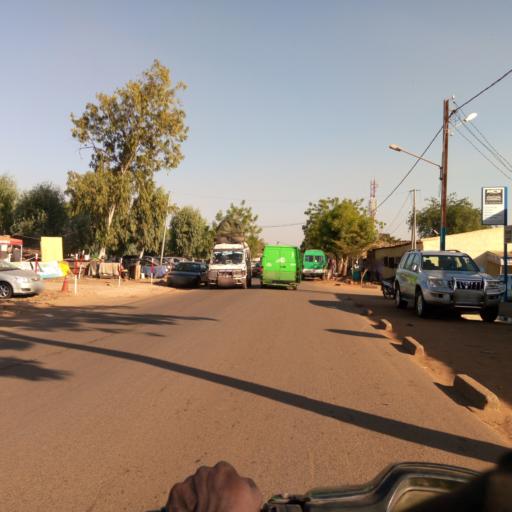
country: ML
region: Bamako
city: Bamako
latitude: 12.6535
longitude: -8.0195
